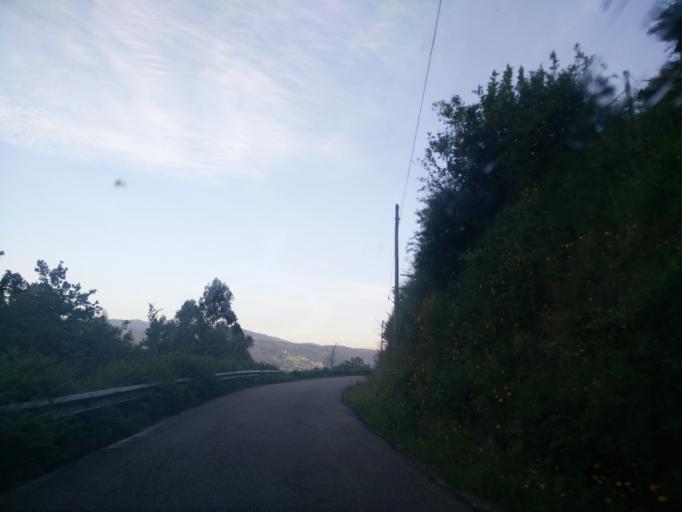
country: ES
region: Galicia
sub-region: Provincia de Pontevedra
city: Mondariz
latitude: 42.2627
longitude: -8.4090
